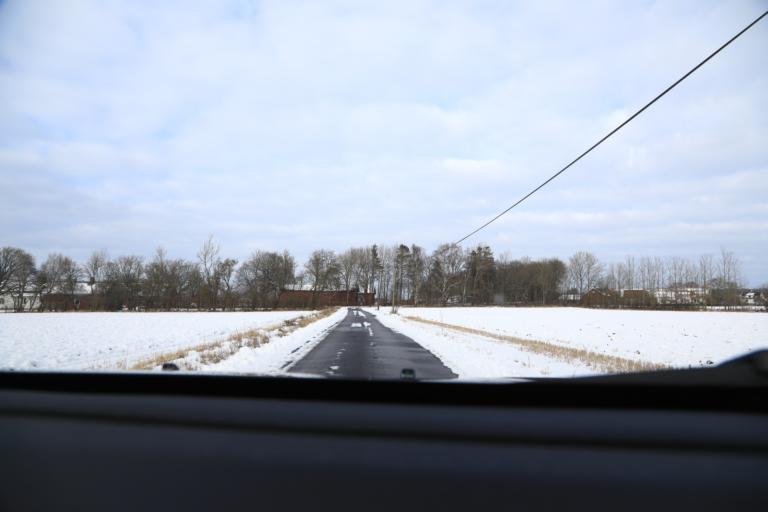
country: SE
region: Halland
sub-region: Kungsbacka Kommun
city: Frillesas
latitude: 57.2292
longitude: 12.1896
